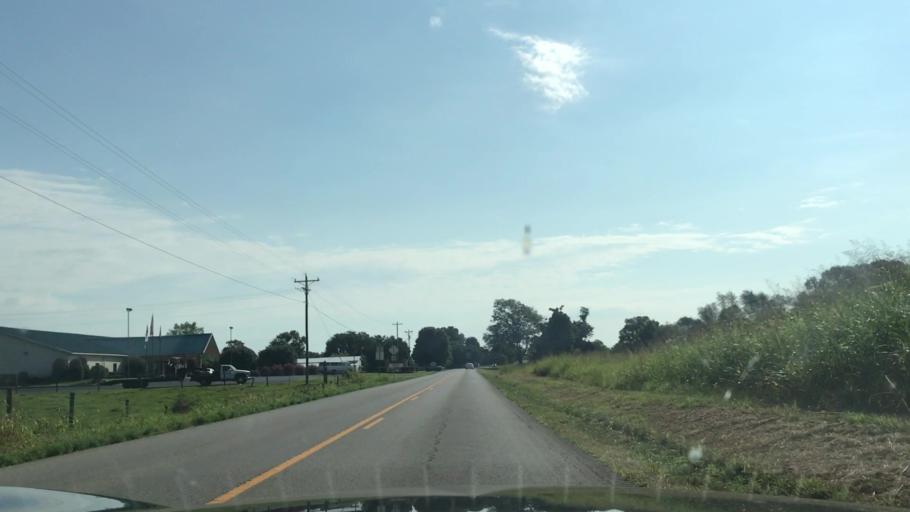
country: US
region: Kentucky
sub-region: Hart County
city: Horse Cave
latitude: 37.1757
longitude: -85.7899
